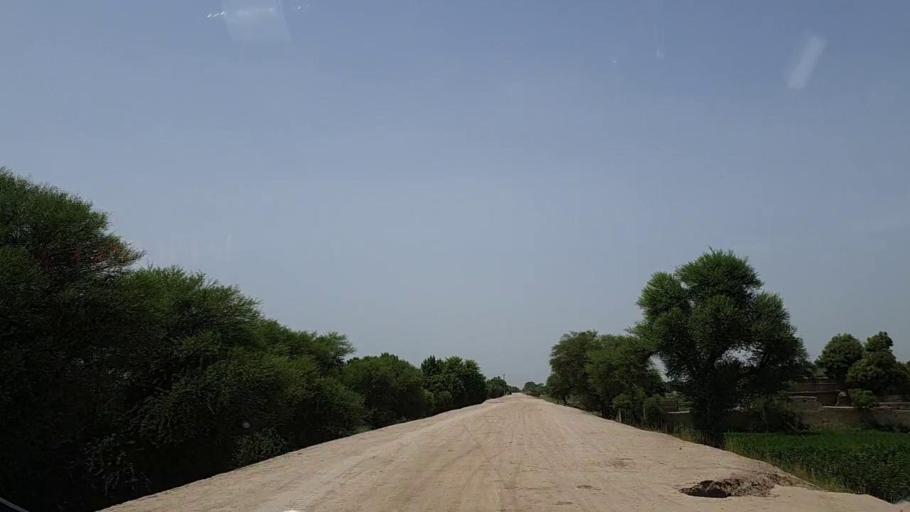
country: PK
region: Sindh
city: Tharu Shah
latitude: 27.0289
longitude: 68.1148
